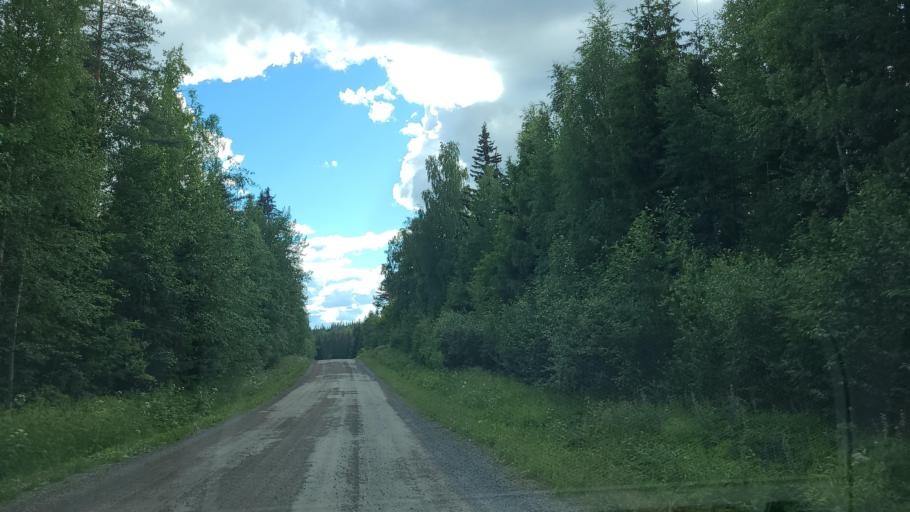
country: FI
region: Central Finland
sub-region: Jaemsae
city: Jaemsae
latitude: 61.9255
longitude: 25.3176
